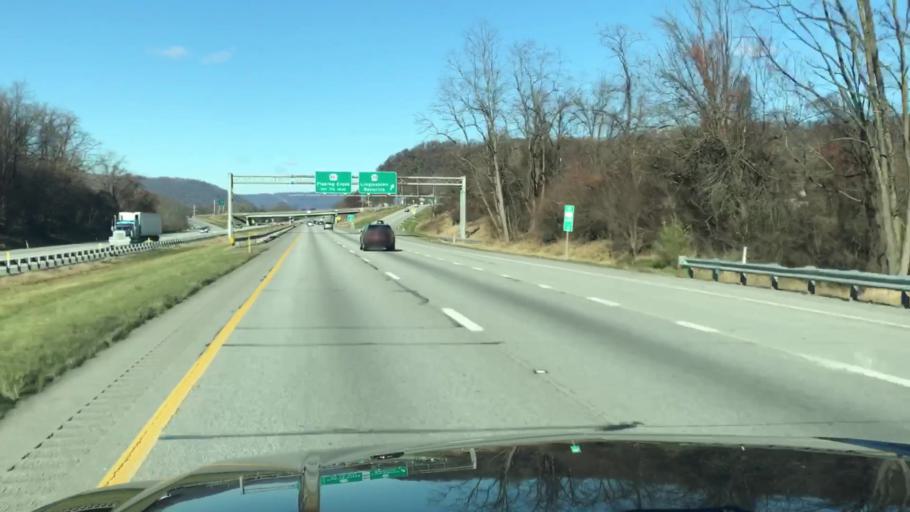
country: US
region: Pennsylvania
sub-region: Perry County
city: Marysville
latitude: 40.3227
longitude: -76.8862
